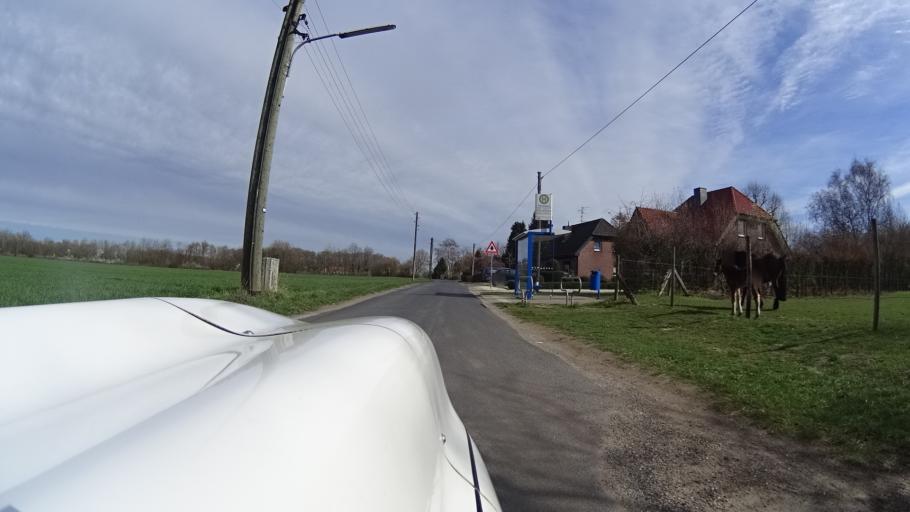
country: NL
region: Limburg
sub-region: Gemeente Gennep
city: Gennep
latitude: 51.6889
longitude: 6.0401
